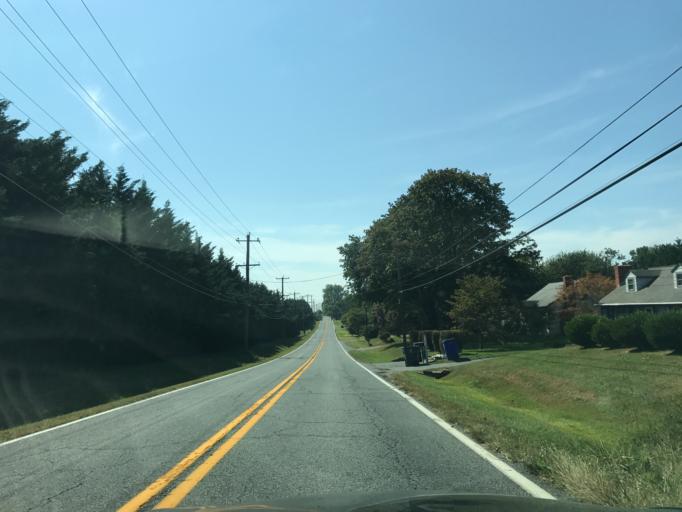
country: US
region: Maryland
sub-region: Cecil County
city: Perryville
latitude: 39.5724
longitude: -76.0451
